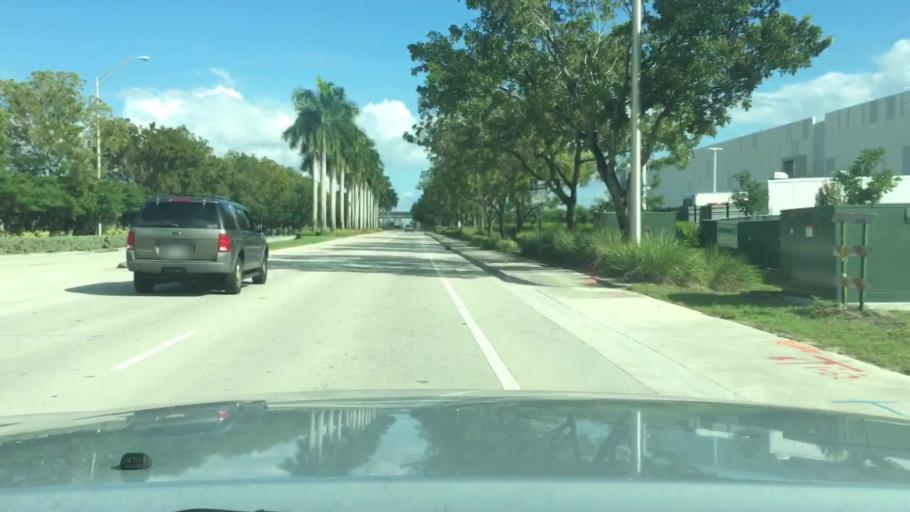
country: US
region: Florida
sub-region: Miami-Dade County
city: Sweetwater
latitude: 25.7967
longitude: -80.3903
